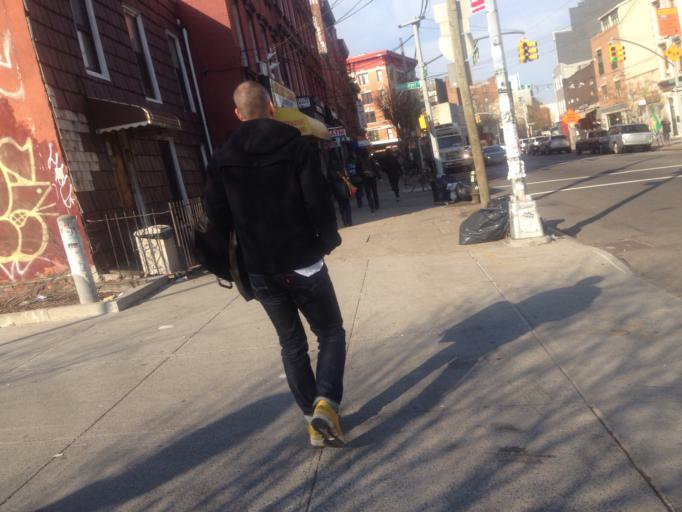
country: US
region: New York
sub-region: Queens County
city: Long Island City
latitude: 40.7141
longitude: -73.9549
